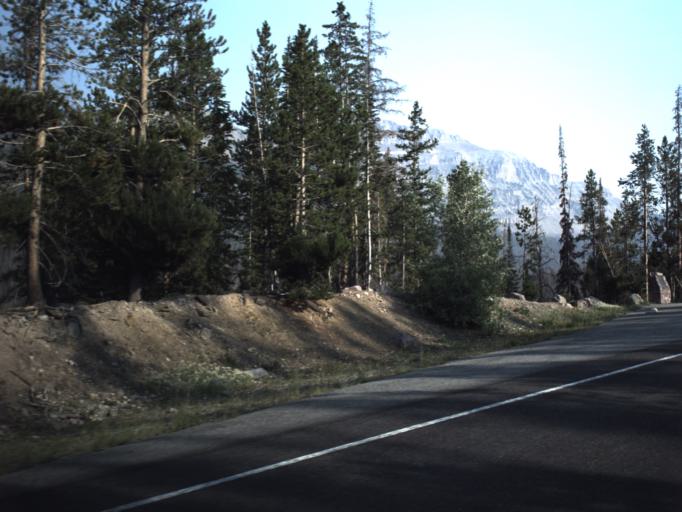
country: US
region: Utah
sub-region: Summit County
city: Kamas
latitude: 40.7585
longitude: -110.8805
